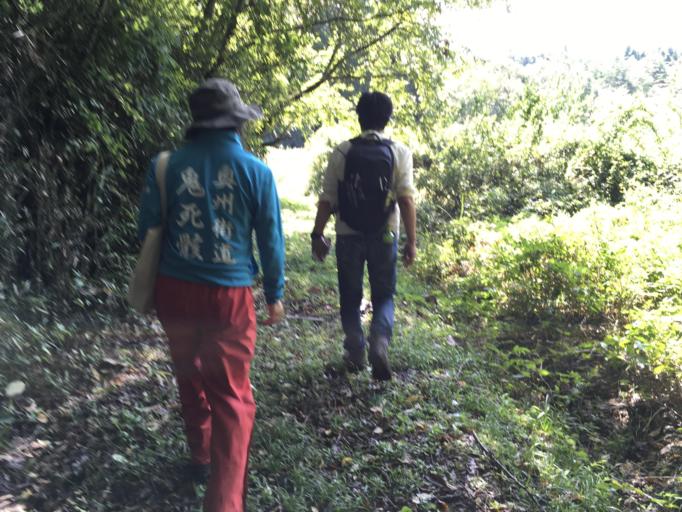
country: JP
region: Iwate
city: Ichinoseki
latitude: 38.8775
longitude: 141.1244
